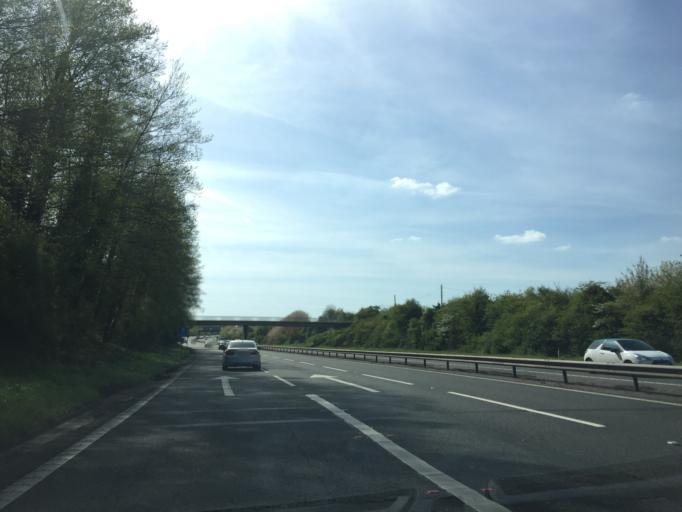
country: GB
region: England
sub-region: Kent
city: Swanley
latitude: 51.3896
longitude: 0.1831
